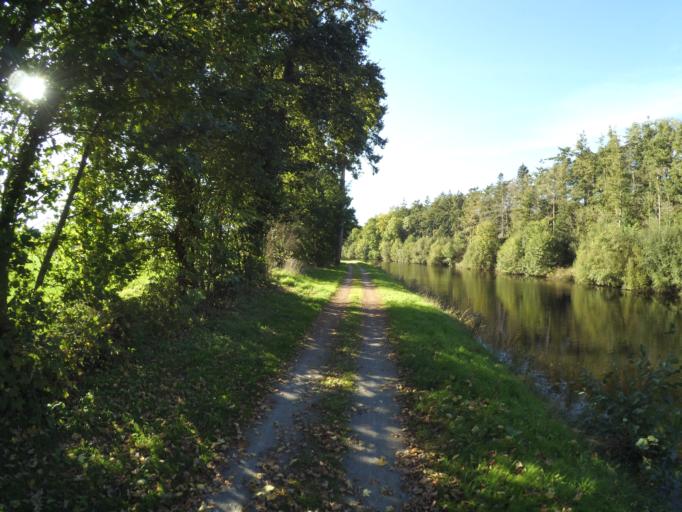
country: FR
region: Brittany
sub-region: Departement du Morbihan
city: Saint-Martin-sur-Oust
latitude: 47.7409
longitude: -2.2347
